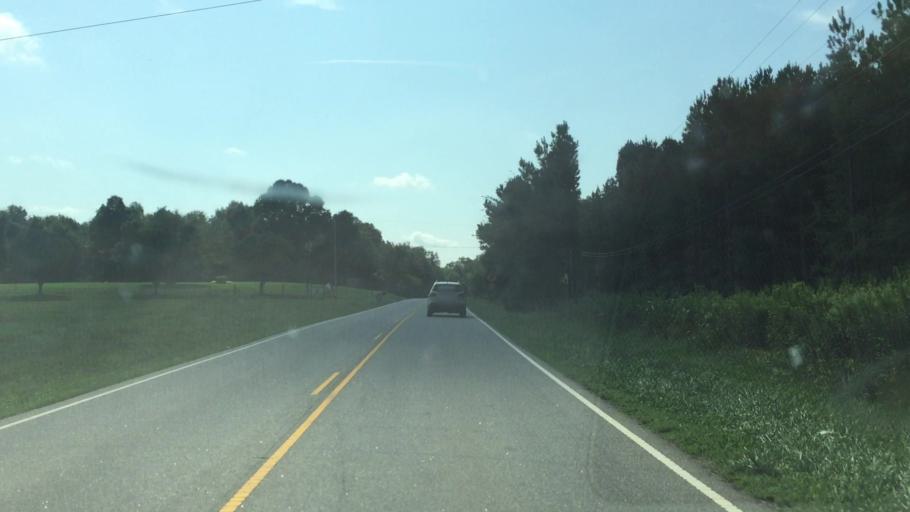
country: US
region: North Carolina
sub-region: Anson County
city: Burnsville
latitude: 35.1215
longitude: -80.3496
